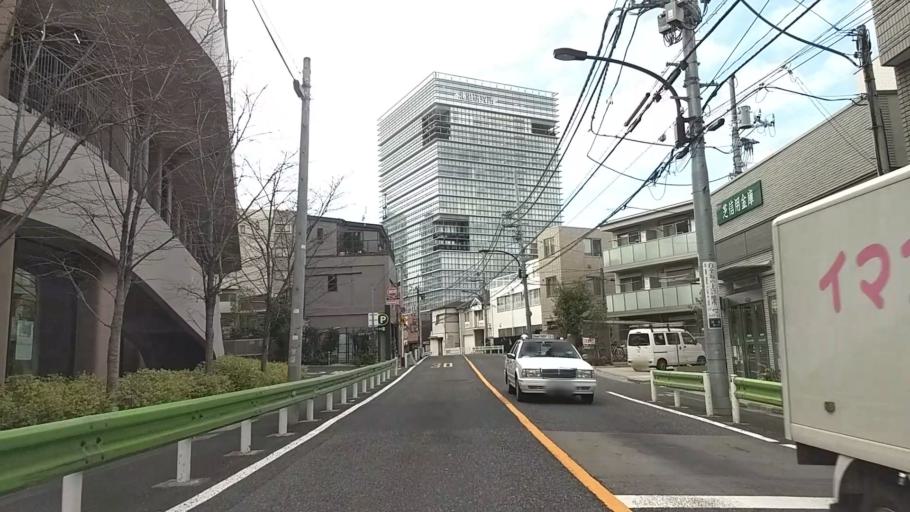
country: JP
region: Tokyo
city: Tokyo
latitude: 35.6440
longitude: 139.7275
